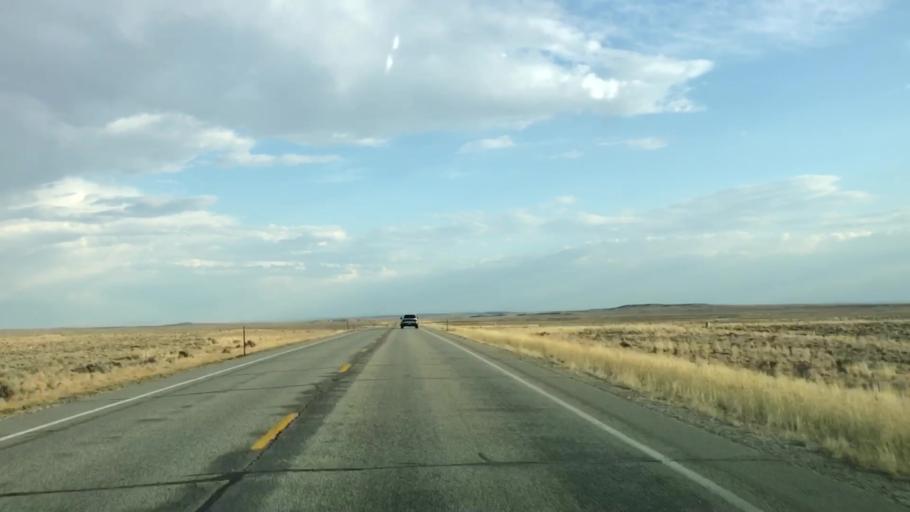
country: US
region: Wyoming
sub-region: Sublette County
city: Pinedale
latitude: 42.3891
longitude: -109.5394
